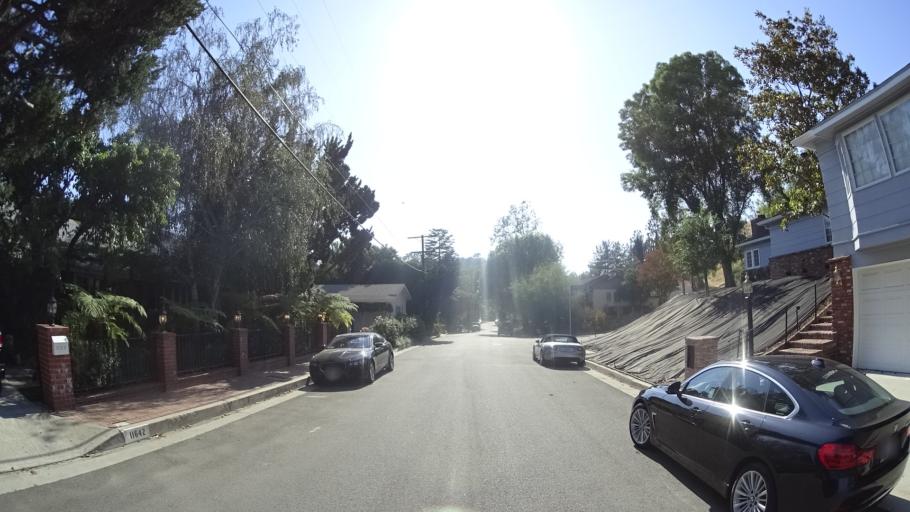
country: US
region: California
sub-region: Los Angeles County
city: Universal City
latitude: 34.1330
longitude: -118.3878
